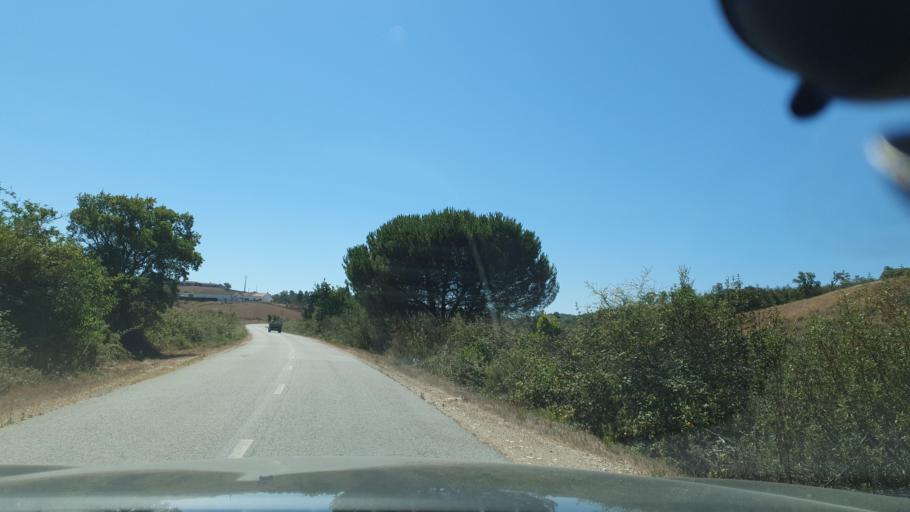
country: PT
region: Beja
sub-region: Odemira
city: Sao Teotonio
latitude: 37.4790
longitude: -8.6296
